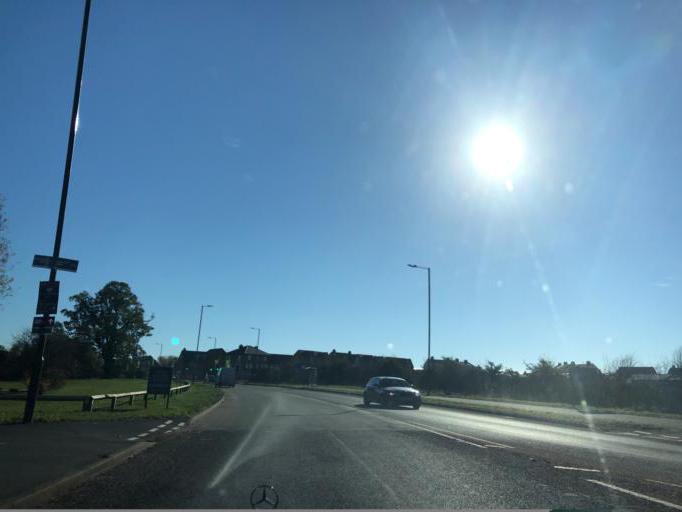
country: GB
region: England
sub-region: Warwickshire
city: Warwick
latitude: 52.2667
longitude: -1.5505
